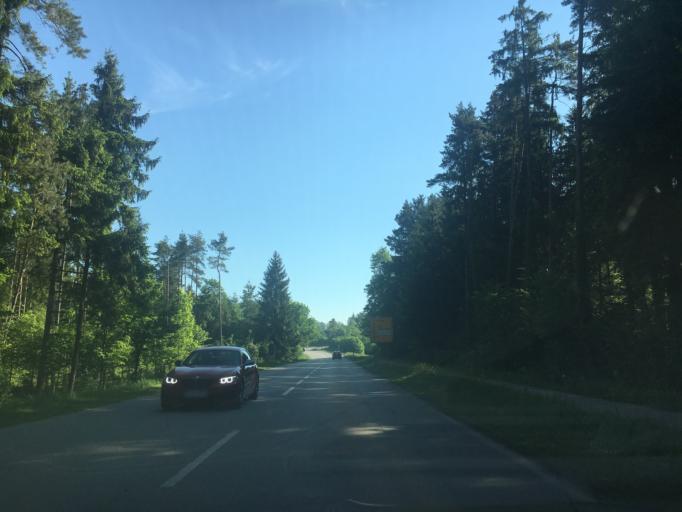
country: DE
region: Bavaria
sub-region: Upper Bavaria
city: Unterneukirchen
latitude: 48.1498
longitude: 12.6100
